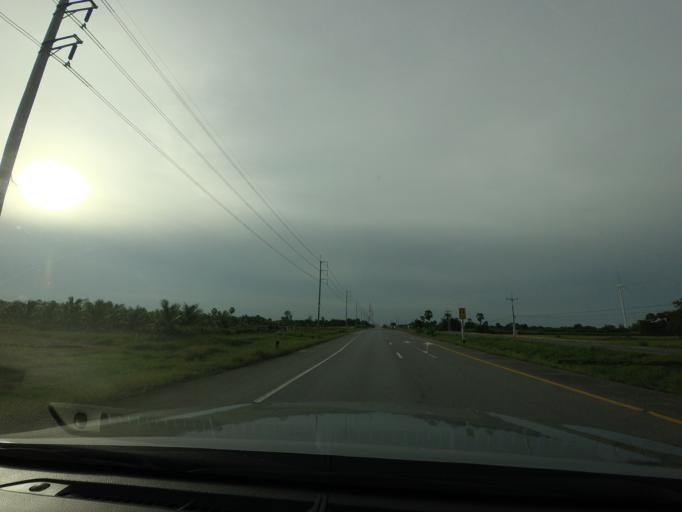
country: TH
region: Nakhon Si Thammarat
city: Hua Sai
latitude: 8.0107
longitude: 100.2978
